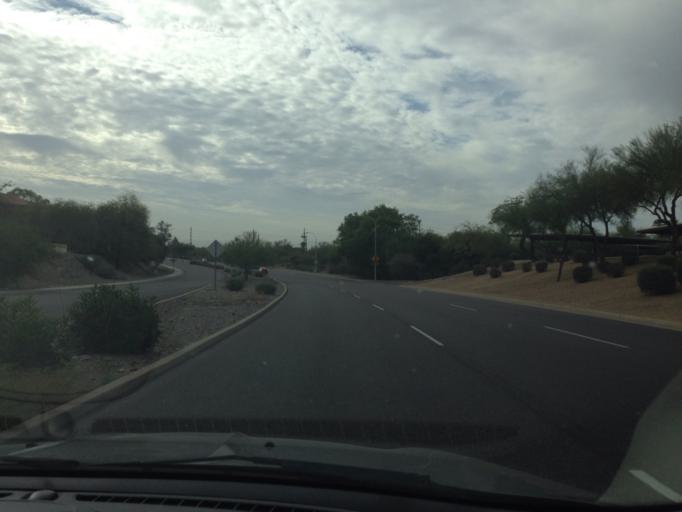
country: US
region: Arizona
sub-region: Maricopa County
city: Paradise Valley
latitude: 33.5284
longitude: -112.0294
